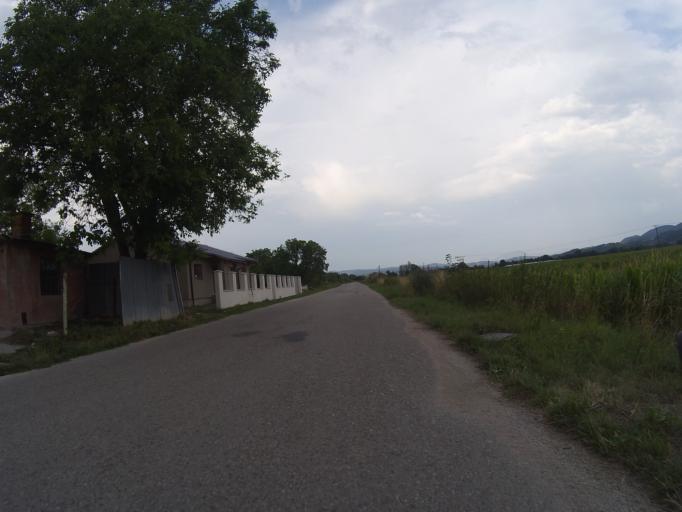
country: SK
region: Nitriansky
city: Ilava
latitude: 49.0387
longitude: 18.2978
